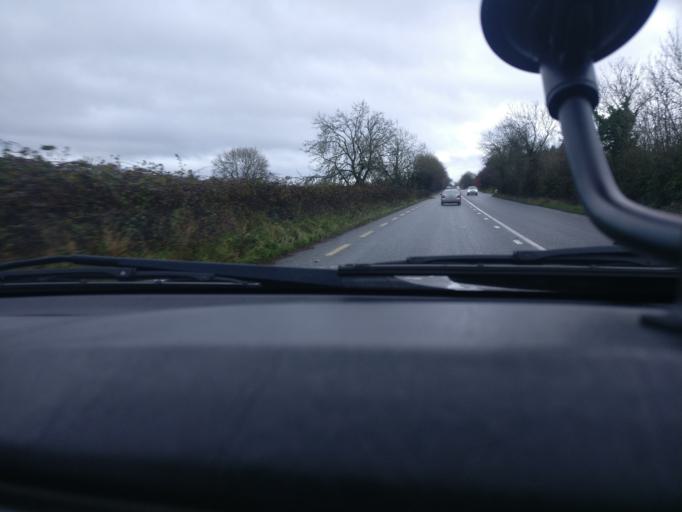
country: IE
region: Leinster
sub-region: Kildare
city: Kilcock
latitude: 53.4172
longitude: -6.7264
